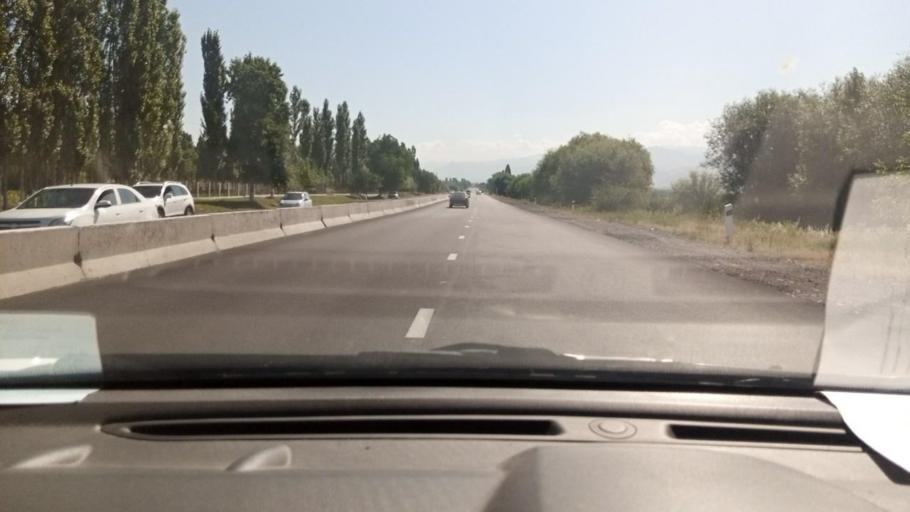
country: UZ
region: Toshkent
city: Angren
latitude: 40.9667
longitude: 69.9698
